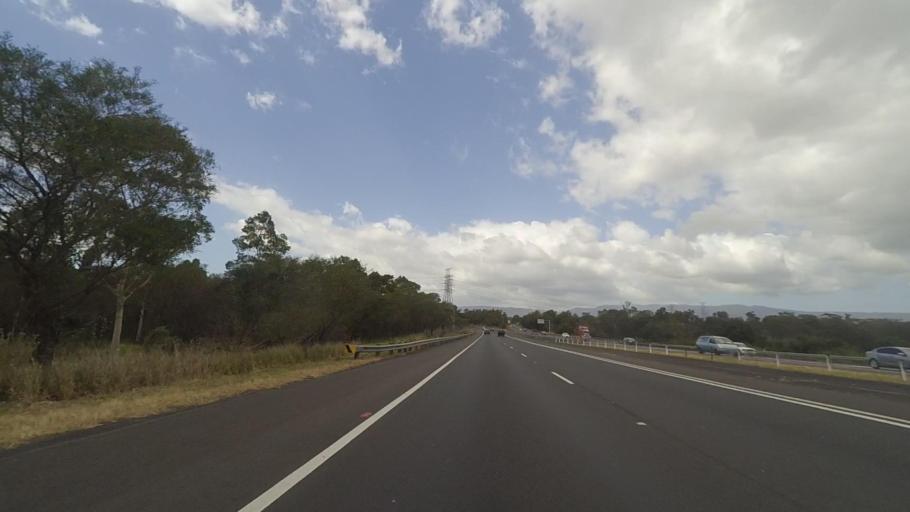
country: AU
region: New South Wales
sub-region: Wollongong
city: Dapto
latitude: -34.5254
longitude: 150.7878
